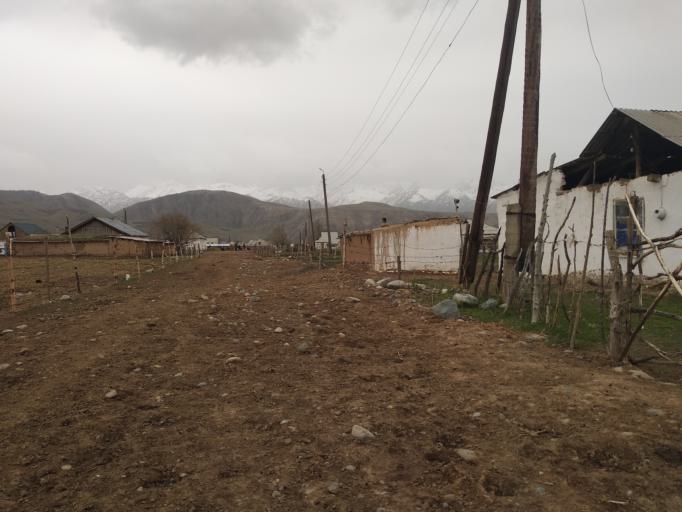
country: KG
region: Naryn
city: Naryn
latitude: 41.5206
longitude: 76.4359
